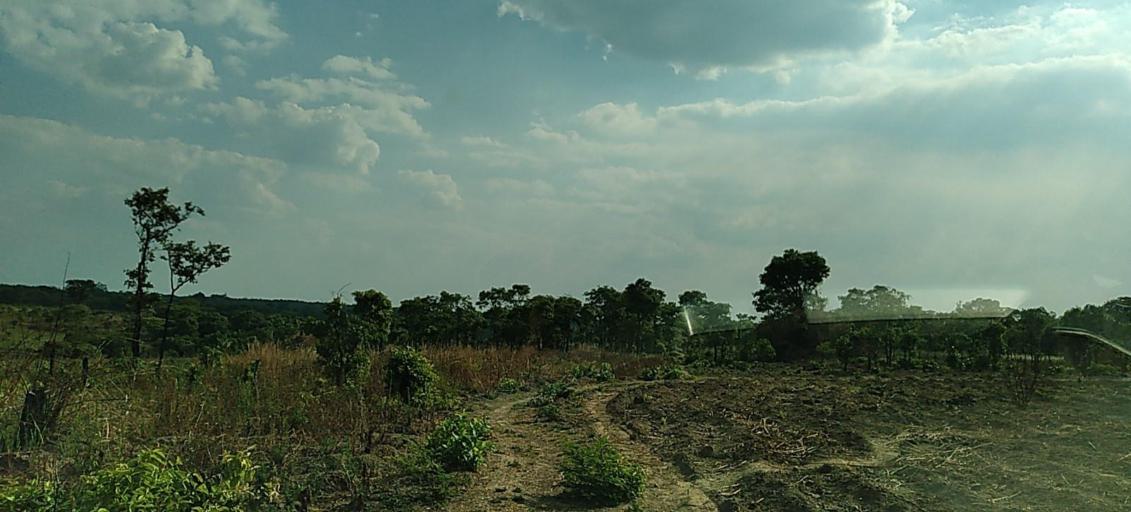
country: ZM
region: Copperbelt
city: Chililabombwe
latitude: -12.3619
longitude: 27.3905
